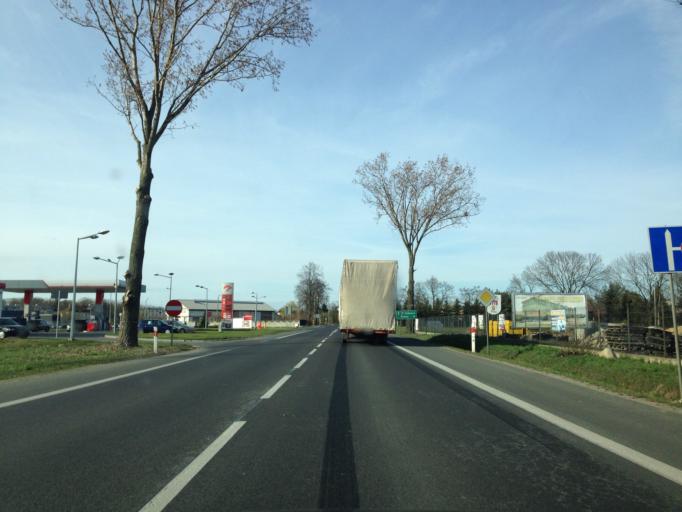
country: PL
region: Kujawsko-Pomorskie
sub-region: Powiat wloclawski
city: Lubien Kujawski
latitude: 52.3961
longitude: 19.1713
